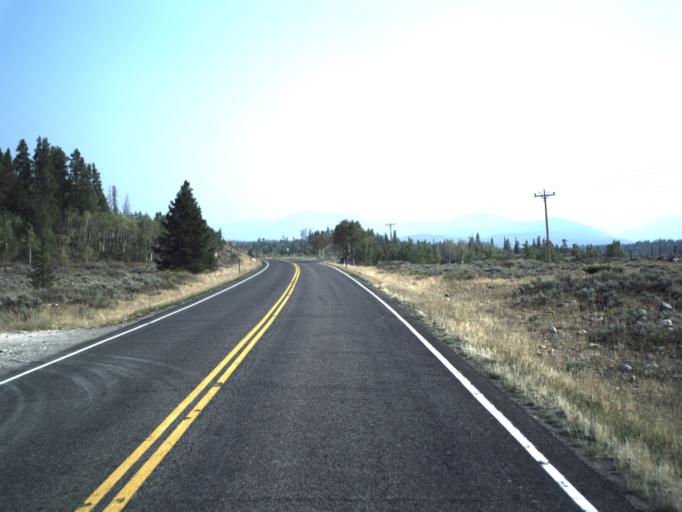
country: US
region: Wyoming
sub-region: Uinta County
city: Evanston
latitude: 40.9349
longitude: -110.8347
